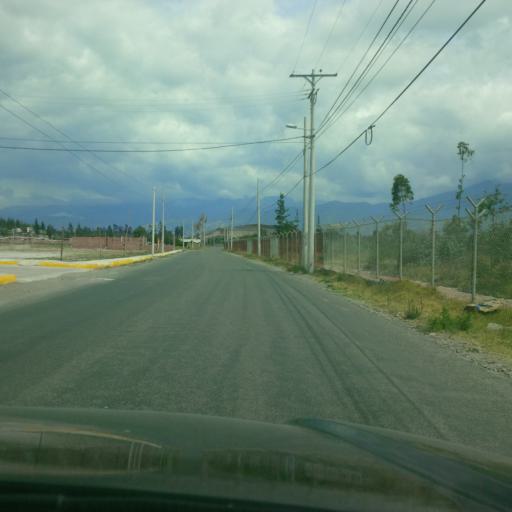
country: EC
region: Chimborazo
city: Riobamba
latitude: -1.6428
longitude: -78.6586
